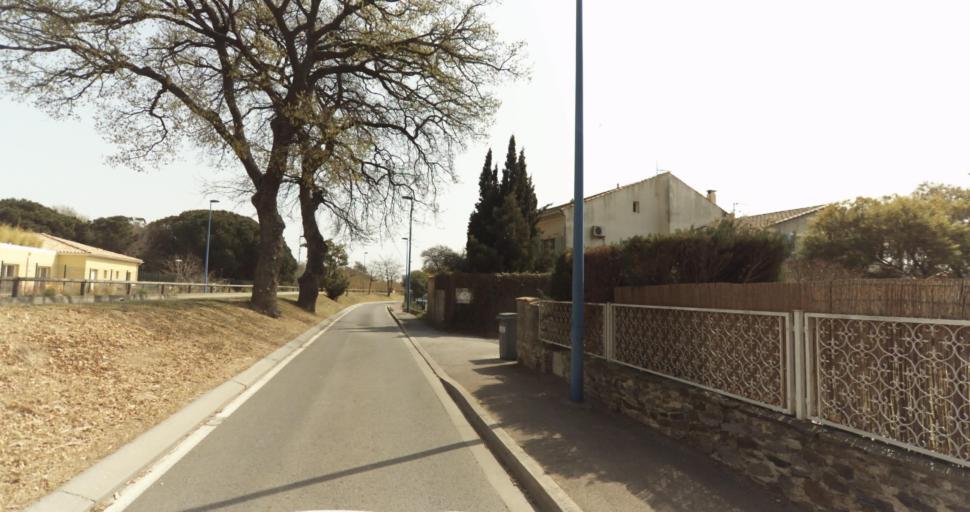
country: FR
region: Provence-Alpes-Cote d'Azur
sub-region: Departement du Var
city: Bormes-les-Mimosas
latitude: 43.1364
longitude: 6.3473
